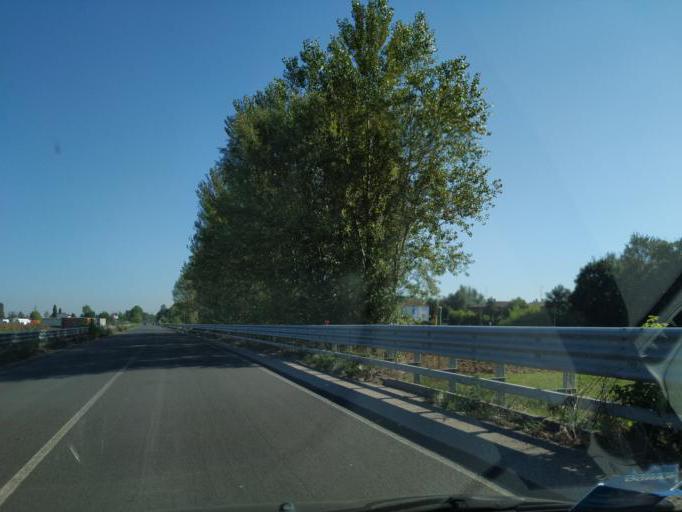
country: IT
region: Emilia-Romagna
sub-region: Provincia di Bologna
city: San Giovanni in Persiceto
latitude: 44.6477
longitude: 11.1742
